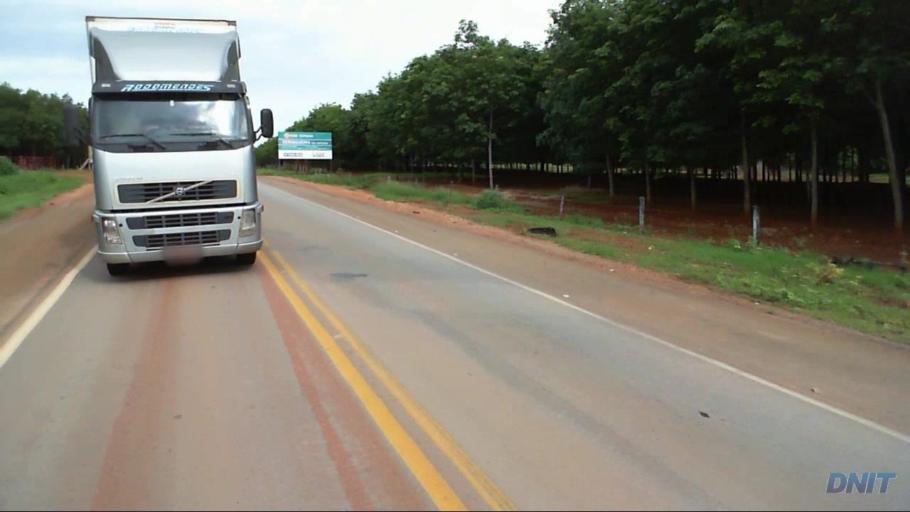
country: BR
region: Goias
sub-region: Barro Alto
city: Barro Alto
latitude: -14.8785
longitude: -48.9929
